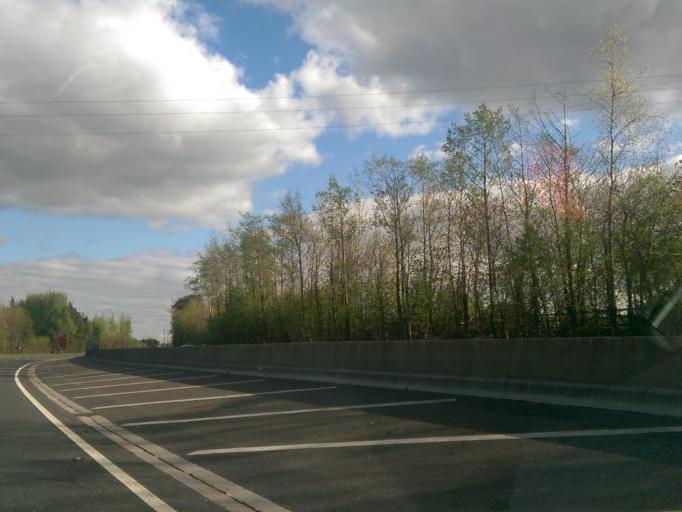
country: IE
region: Leinster
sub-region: An Iarmhi
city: Athlone
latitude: 53.4245
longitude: -7.8939
